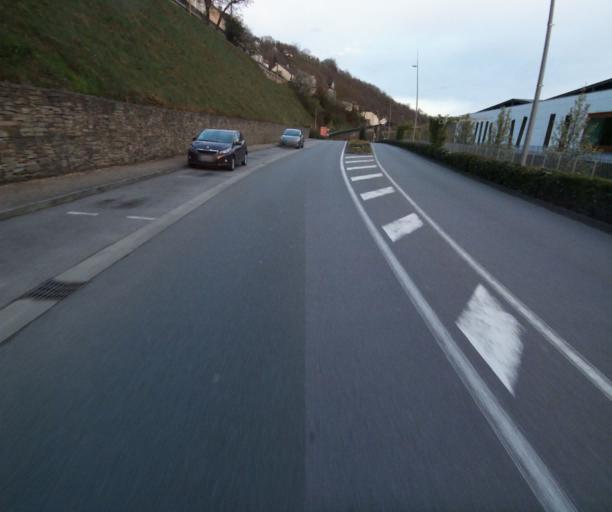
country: FR
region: Limousin
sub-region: Departement de la Correze
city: Tulle
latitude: 45.2583
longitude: 1.7584
